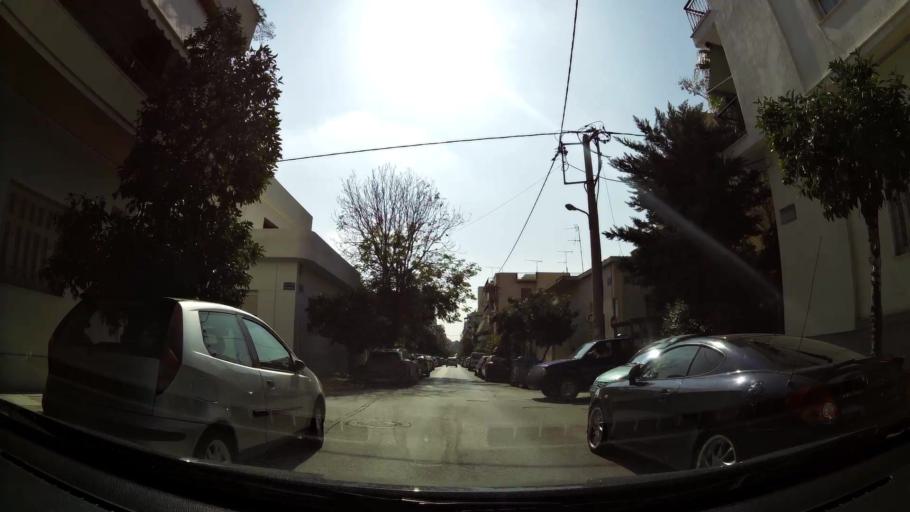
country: GR
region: Attica
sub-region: Nomos Piraios
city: Keratsini
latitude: 37.9601
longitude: 23.6286
